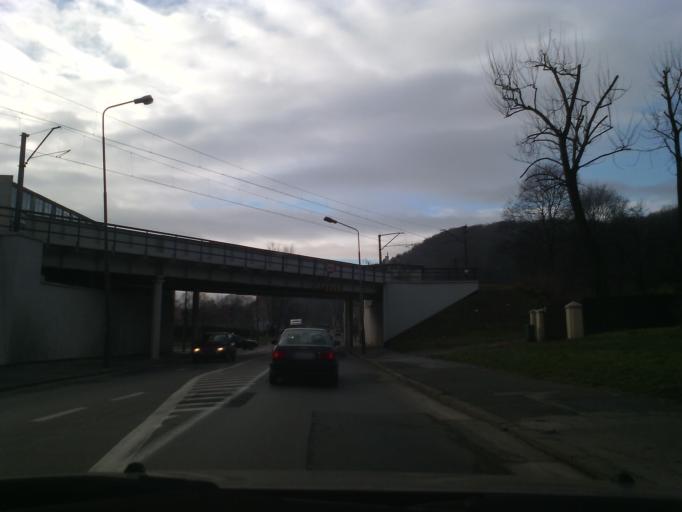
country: PL
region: Lower Silesian Voivodeship
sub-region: Powiat walbrzyski
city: Walbrzych
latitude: 50.7990
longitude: 16.2907
